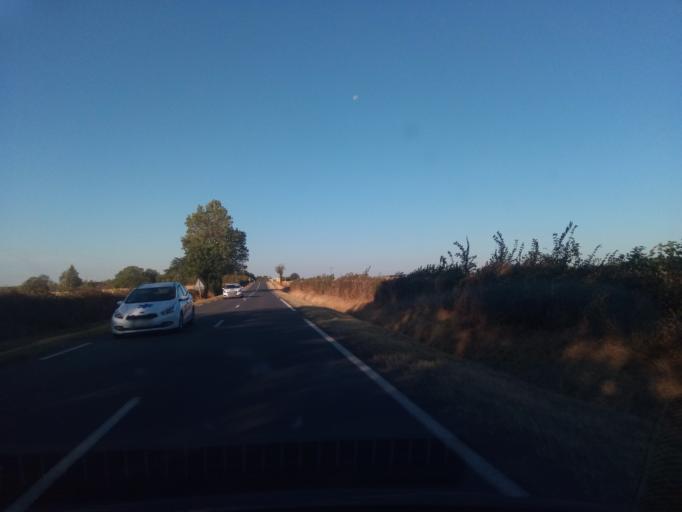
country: FR
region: Poitou-Charentes
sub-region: Departement de la Vienne
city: Lussac-les-Chateaux
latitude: 46.4040
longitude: 0.7807
